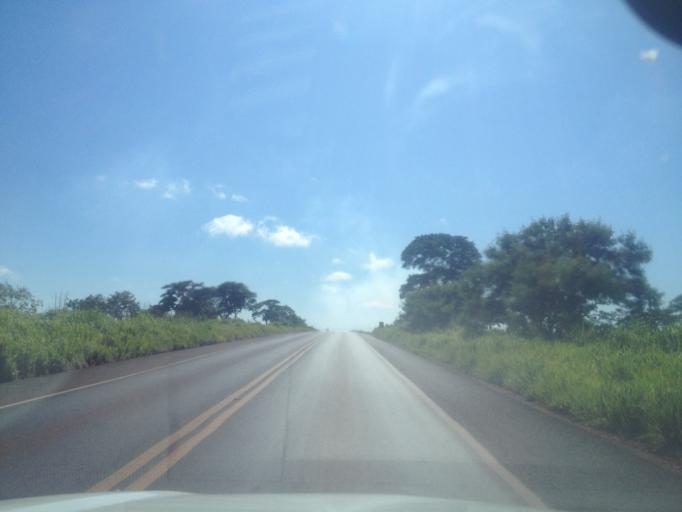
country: BR
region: Minas Gerais
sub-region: Santa Vitoria
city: Santa Vitoria
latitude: -19.0474
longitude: -50.4837
